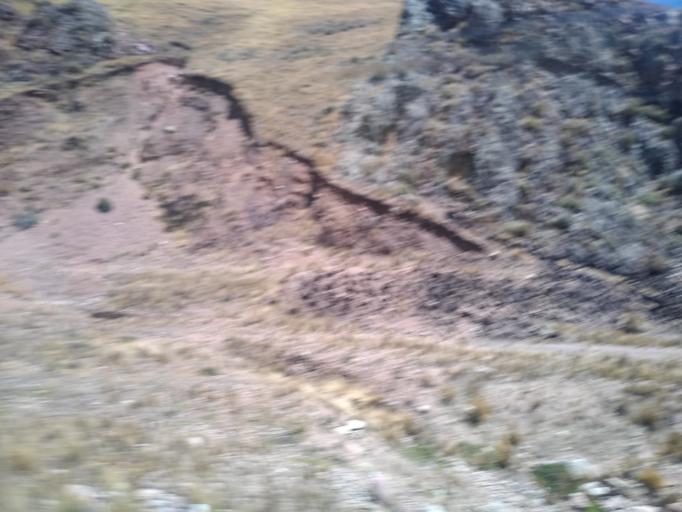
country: PE
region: Cusco
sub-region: Provincia de Canas
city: Layo
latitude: -14.4813
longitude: -71.0058
